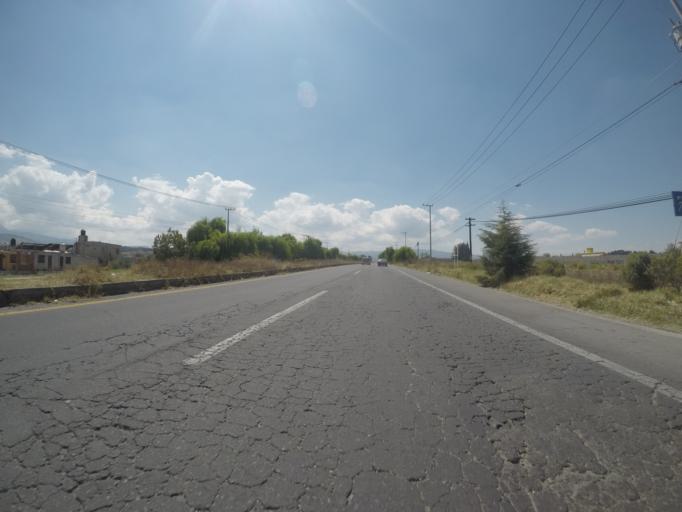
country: MX
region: Mexico
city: Santa Cruz Cuauhtenco
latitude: 19.2537
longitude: -99.7334
